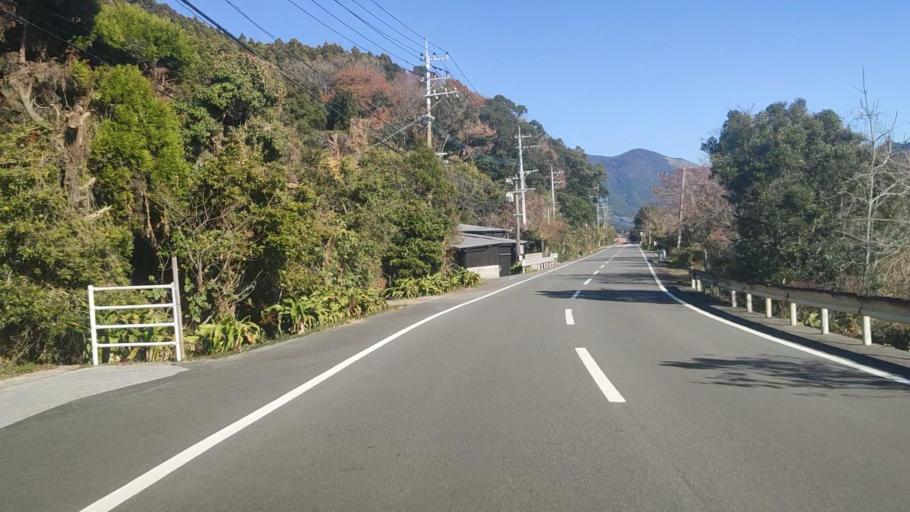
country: JP
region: Oita
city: Saiki
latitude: 32.7979
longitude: 131.8867
